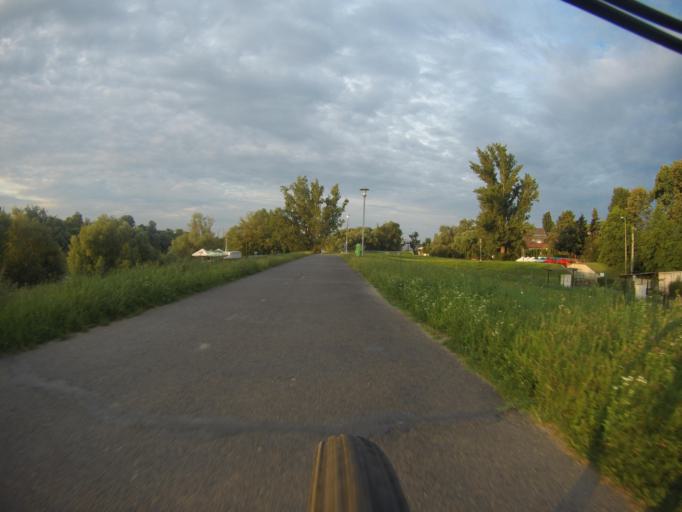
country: HU
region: Pest
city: Budakalasz
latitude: 47.5953
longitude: 19.0699
